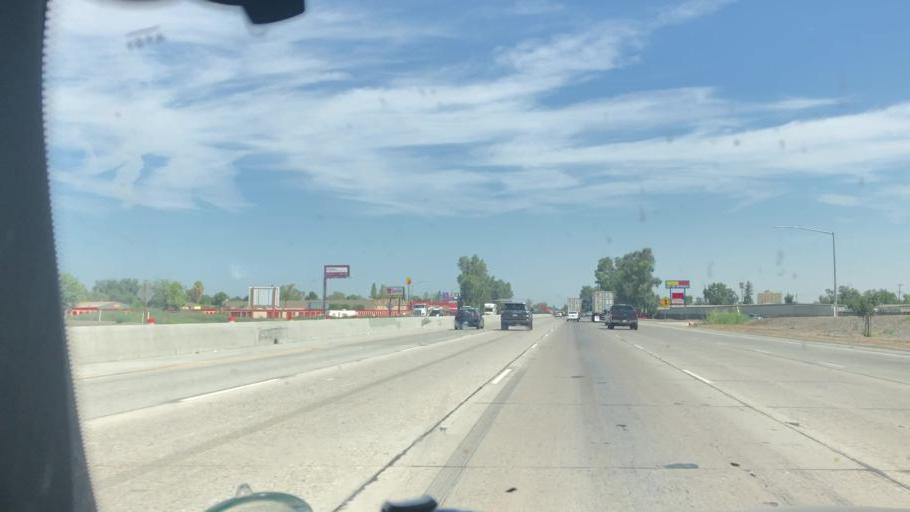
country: US
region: California
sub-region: Kern County
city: Bakersfield
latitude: 35.3179
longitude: -119.0361
